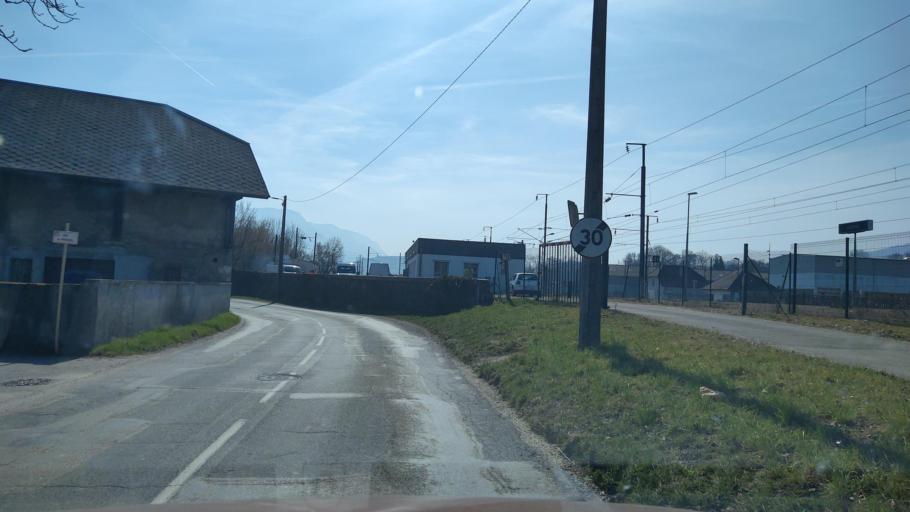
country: FR
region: Rhone-Alpes
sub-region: Departement de la Savoie
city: Albens
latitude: 45.7854
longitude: 5.9489
